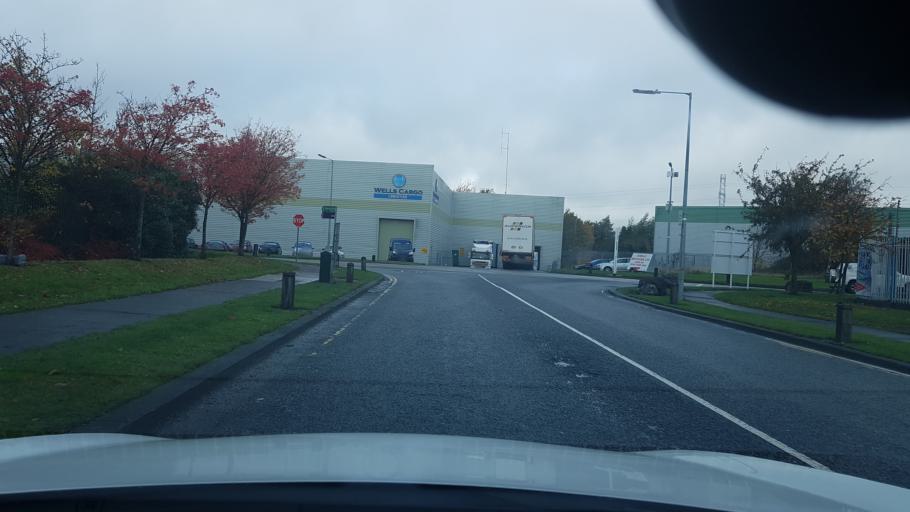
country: IE
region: Leinster
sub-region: Fingal County
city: Blanchardstown
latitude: 53.4040
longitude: -6.3521
